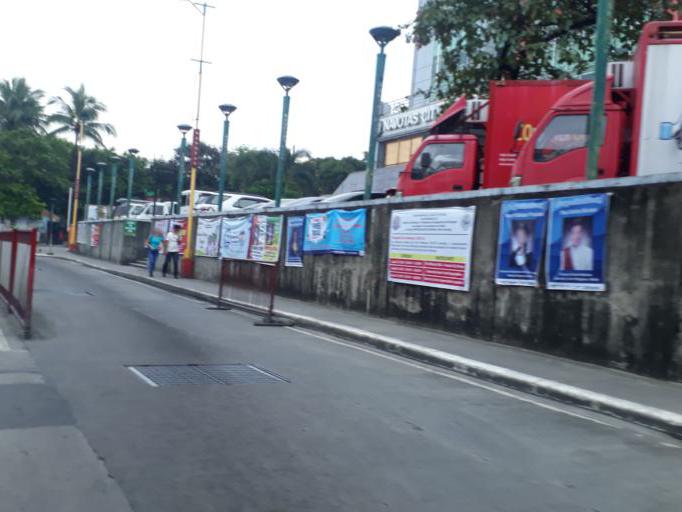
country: PH
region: Calabarzon
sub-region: Province of Rizal
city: Navotas
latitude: 14.6575
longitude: 120.9476
